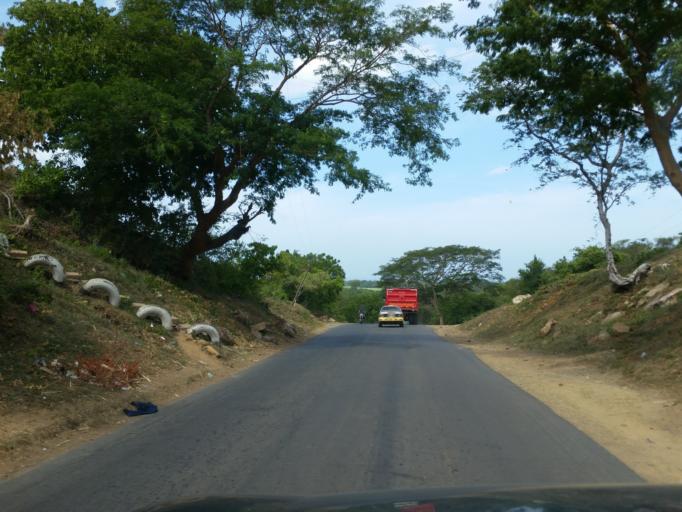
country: NI
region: Managua
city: Masachapa
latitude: 11.8116
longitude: -86.4894
